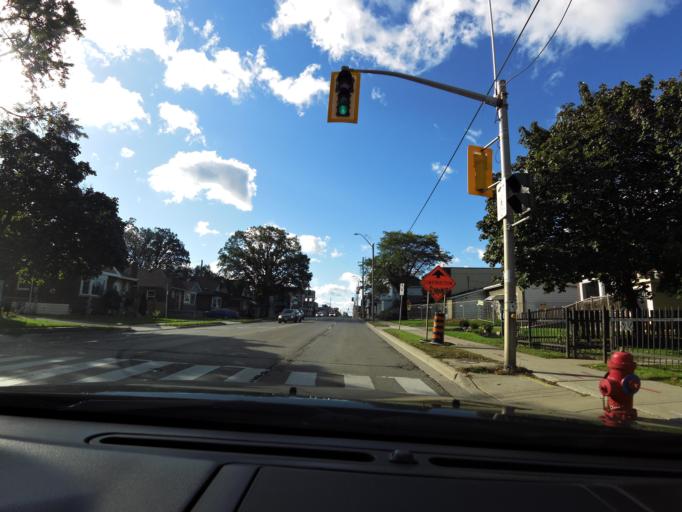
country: CA
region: Ontario
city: Hamilton
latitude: 43.2423
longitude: -79.8759
